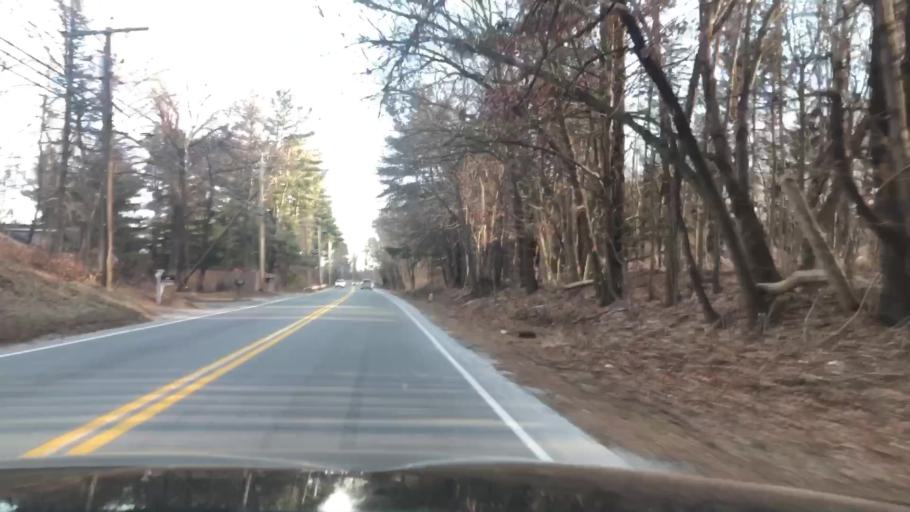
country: US
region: Massachusetts
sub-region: Worcester County
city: Bolton
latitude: 42.4442
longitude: -71.6235
